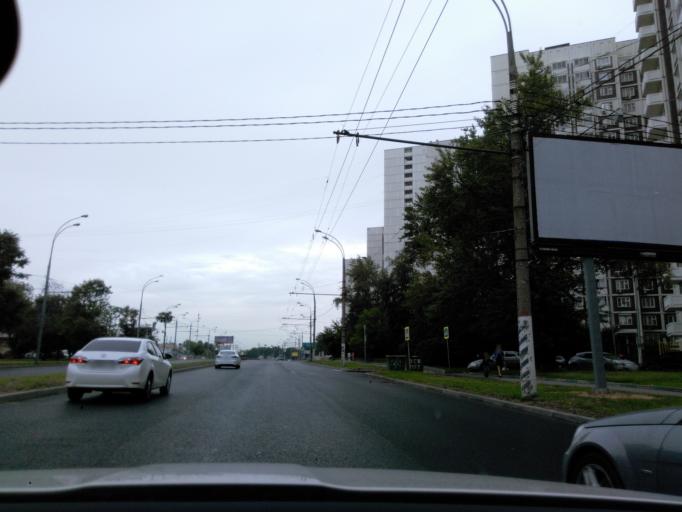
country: RU
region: Moscow
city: Tsaritsyno
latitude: 55.6462
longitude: 37.6567
